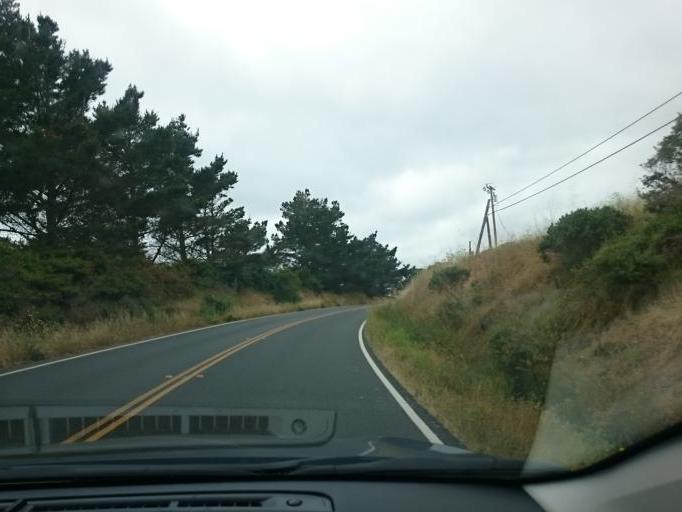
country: US
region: California
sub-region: Marin County
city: Inverness
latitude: 38.1494
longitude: -122.8863
